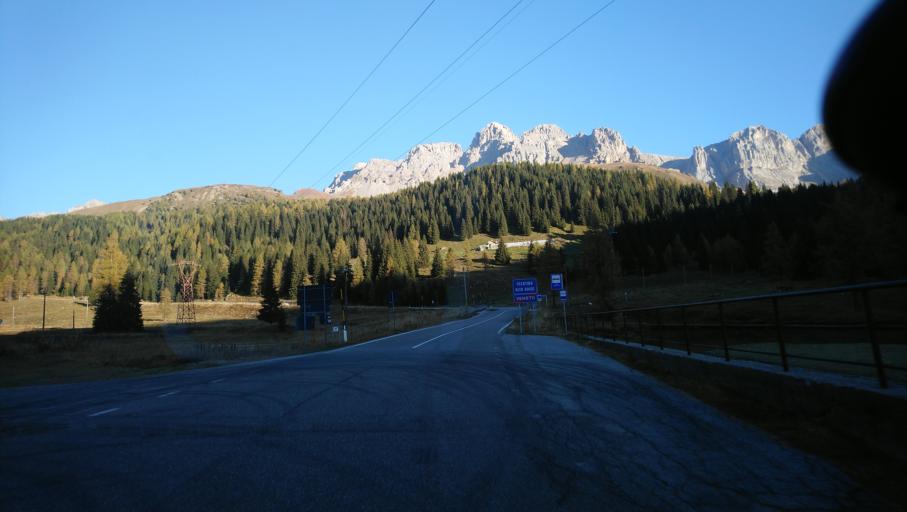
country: IT
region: Veneto
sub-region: Provincia di Belluno
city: Falcade Alto
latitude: 46.3764
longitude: 11.8205
